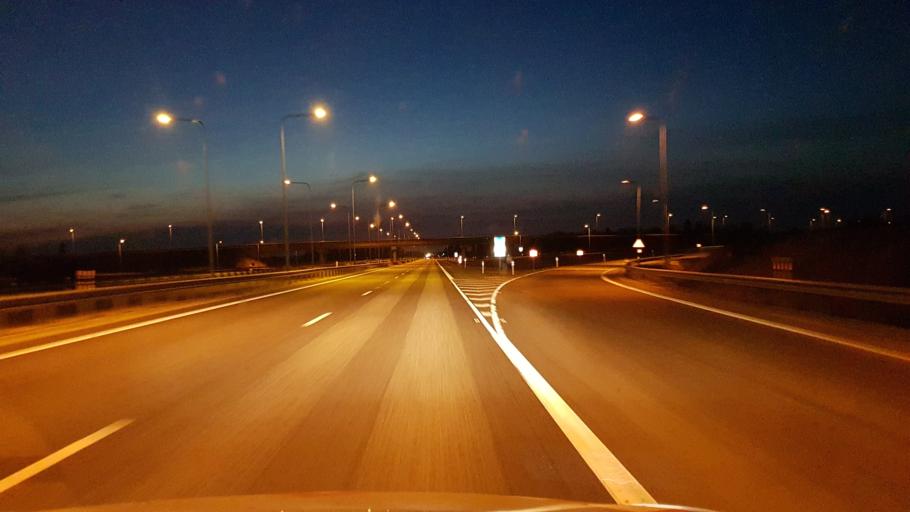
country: EE
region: Harju
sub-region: Rae vald
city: Vaida
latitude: 59.2497
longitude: 25.0173
